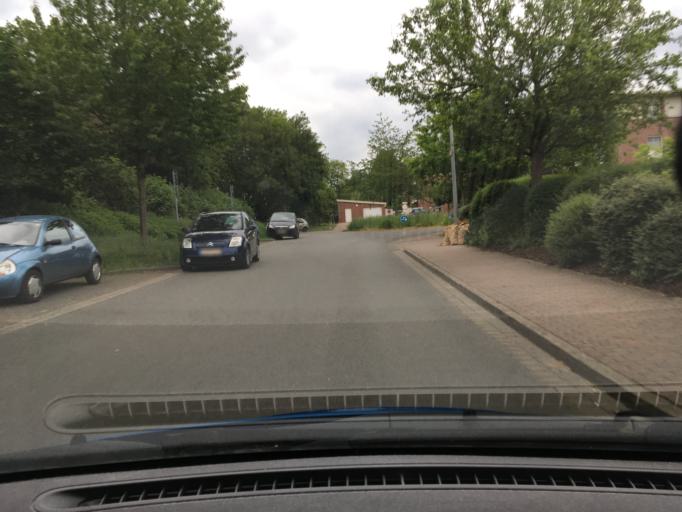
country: DE
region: Lower Saxony
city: Lueneburg
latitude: 53.2511
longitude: 10.3867
